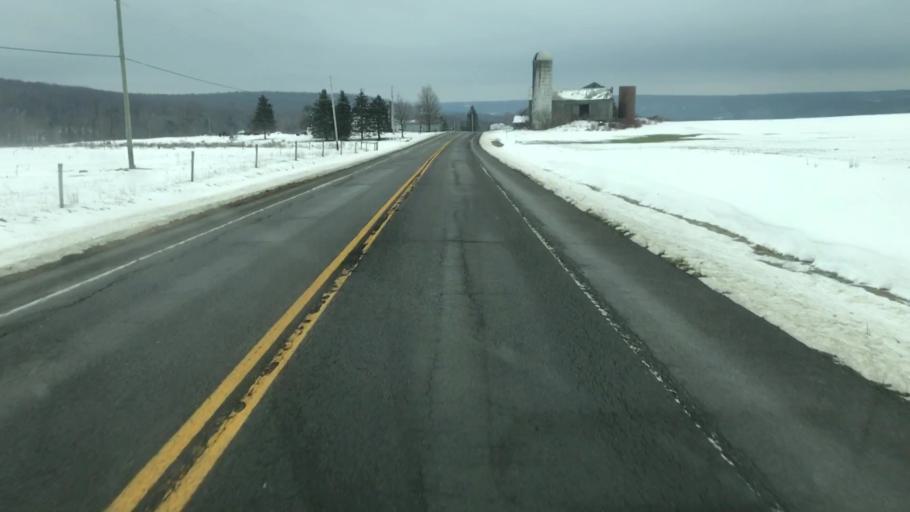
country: US
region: New York
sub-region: Cayuga County
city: Moravia
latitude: 42.7203
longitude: -76.3136
